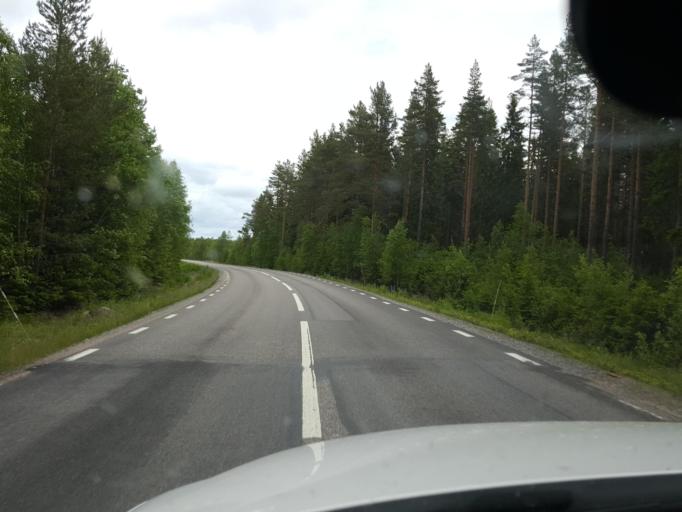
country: SE
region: Gaevleborg
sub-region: Ljusdals Kommun
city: Farila
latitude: 61.7931
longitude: 15.6988
